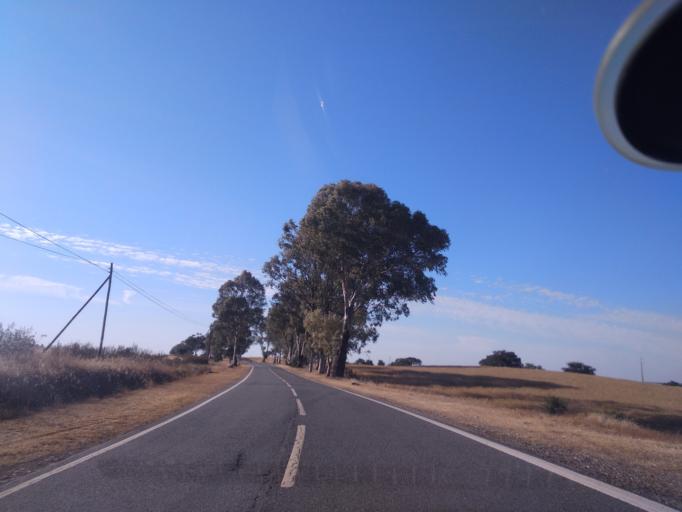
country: PT
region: Beja
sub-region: Almodovar
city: Almodovar
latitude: 37.4514
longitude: -7.9961
